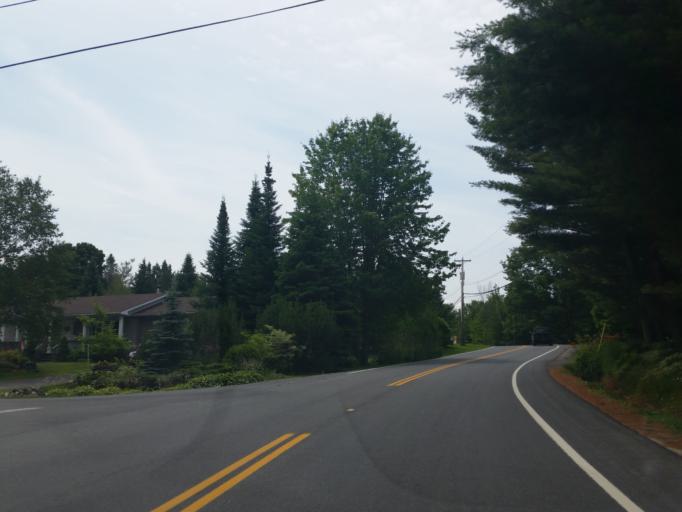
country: CA
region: Ontario
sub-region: Parry Sound District
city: Parry Sound
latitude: 45.3921
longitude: -80.0276
